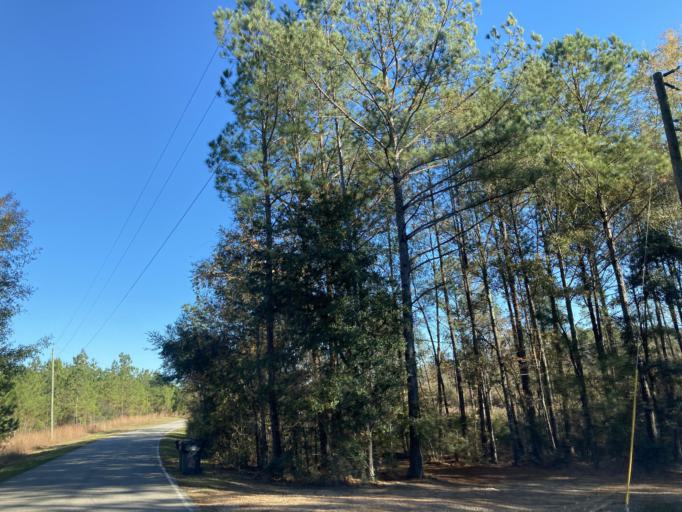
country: US
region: Mississippi
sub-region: Lamar County
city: Sumrall
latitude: 31.3716
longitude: -89.5839
